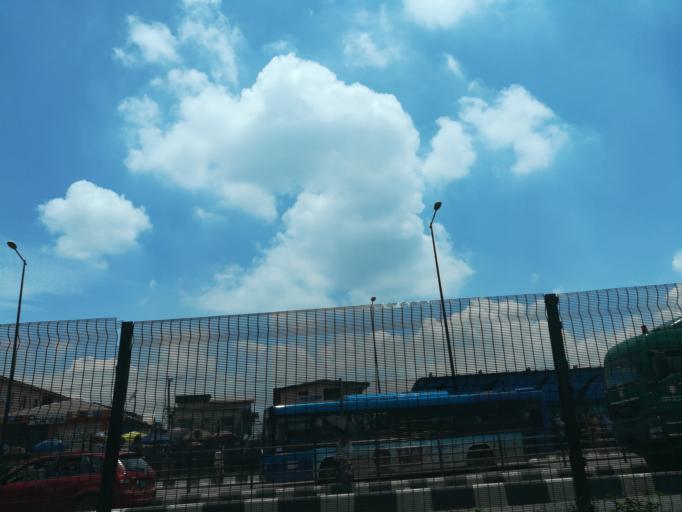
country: NG
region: Lagos
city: Ikorodu
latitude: 6.6213
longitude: 3.5013
